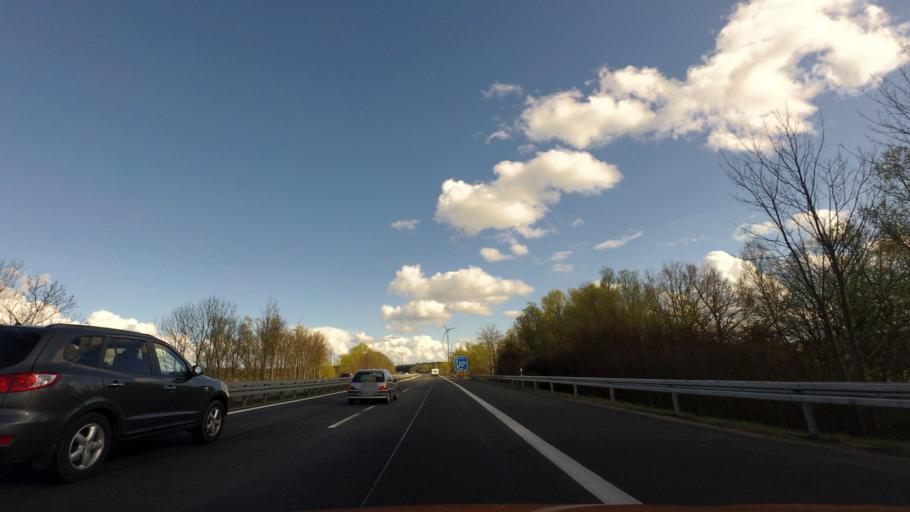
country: DE
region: Brandenburg
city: Gerdshagen
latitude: 53.2397
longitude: 12.1896
